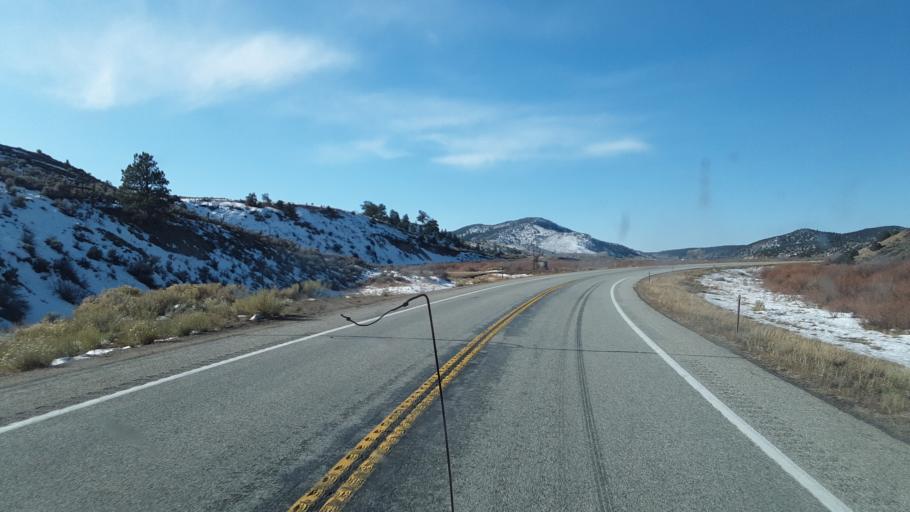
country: US
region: Colorado
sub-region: Costilla County
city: San Luis
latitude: 37.5166
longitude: -105.3014
